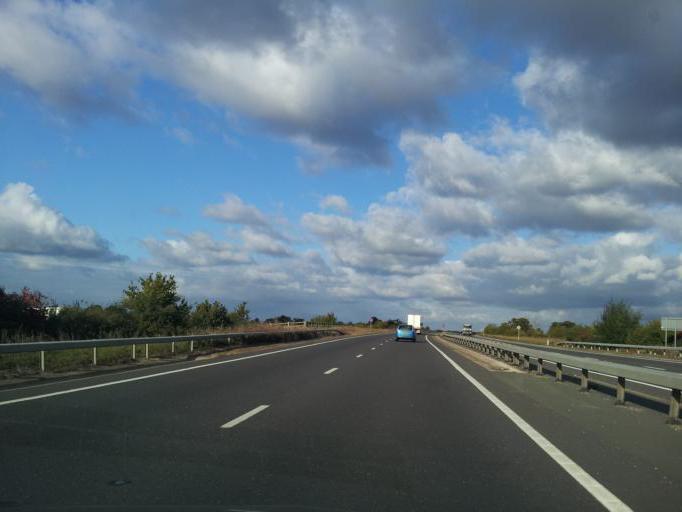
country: GB
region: England
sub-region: Bedford
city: Willington
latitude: 52.1579
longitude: -0.3776
